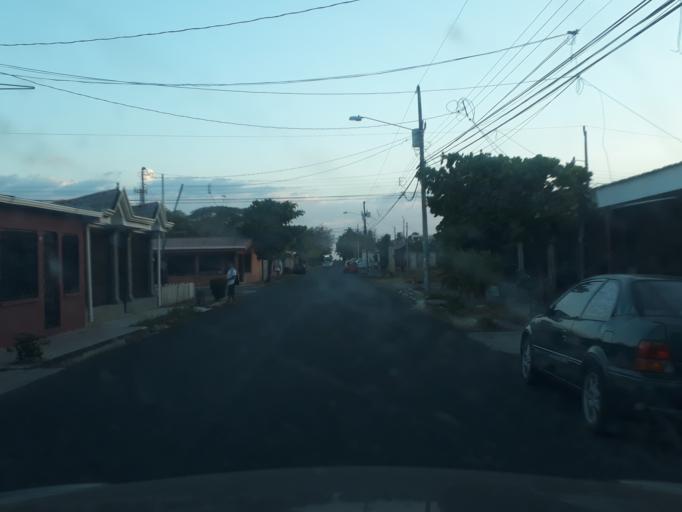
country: CR
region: Puntarenas
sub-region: Canton Central de Puntarenas
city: Chacarita
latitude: 9.9767
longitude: -84.7478
